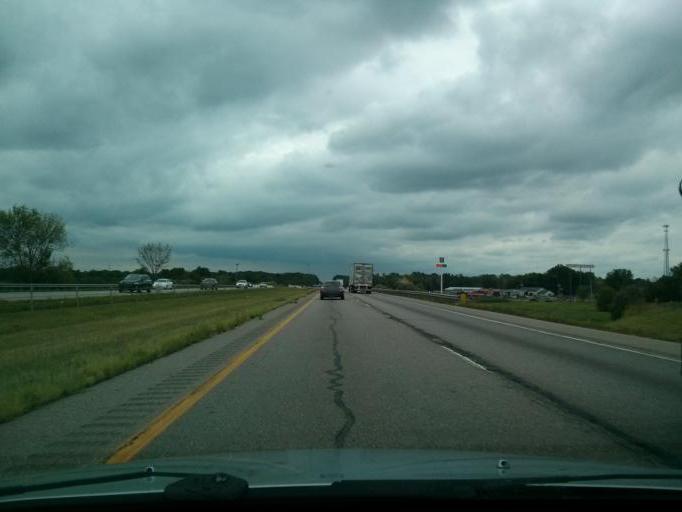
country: US
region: Ohio
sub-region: Portage County
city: Ravenna
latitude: 41.1057
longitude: -81.1595
